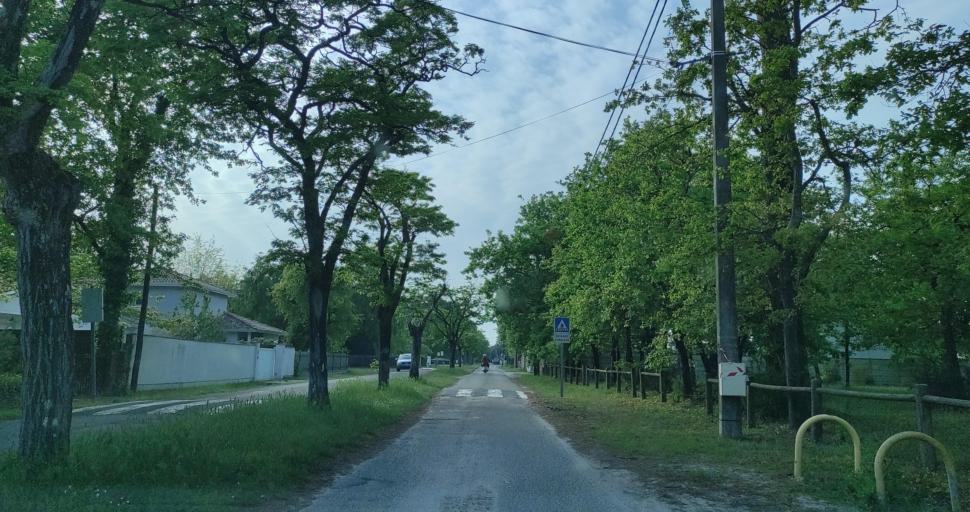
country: FR
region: Aquitaine
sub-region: Departement de la Gironde
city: Ares
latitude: 44.7528
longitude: -1.1264
